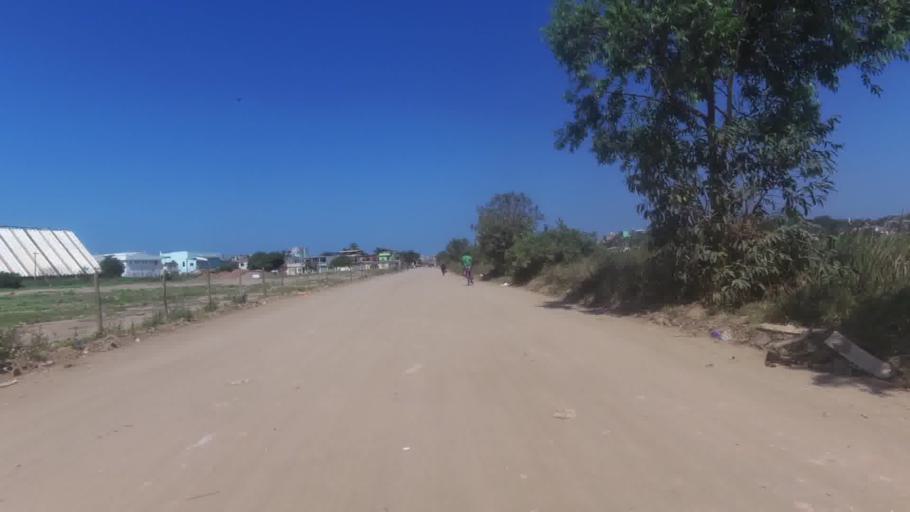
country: BR
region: Espirito Santo
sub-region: Itapemirim
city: Itapemirim
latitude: -21.0127
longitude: -40.8162
